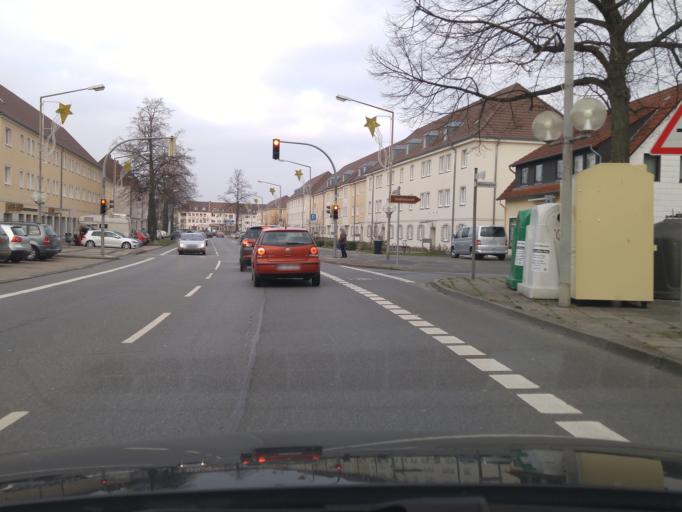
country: DE
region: Lower Saxony
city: Wolfsburg
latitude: 52.4220
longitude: 10.7928
